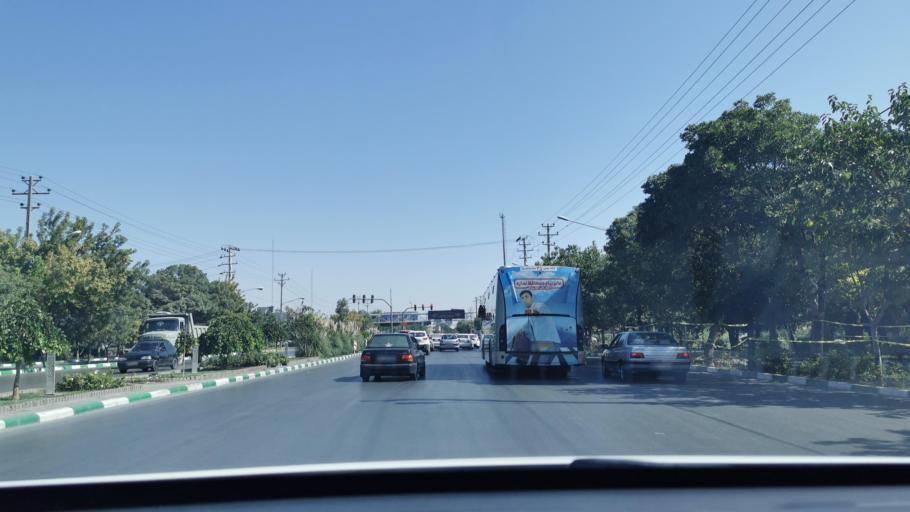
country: IR
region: Razavi Khorasan
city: Mashhad
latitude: 36.3340
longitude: 59.6255
